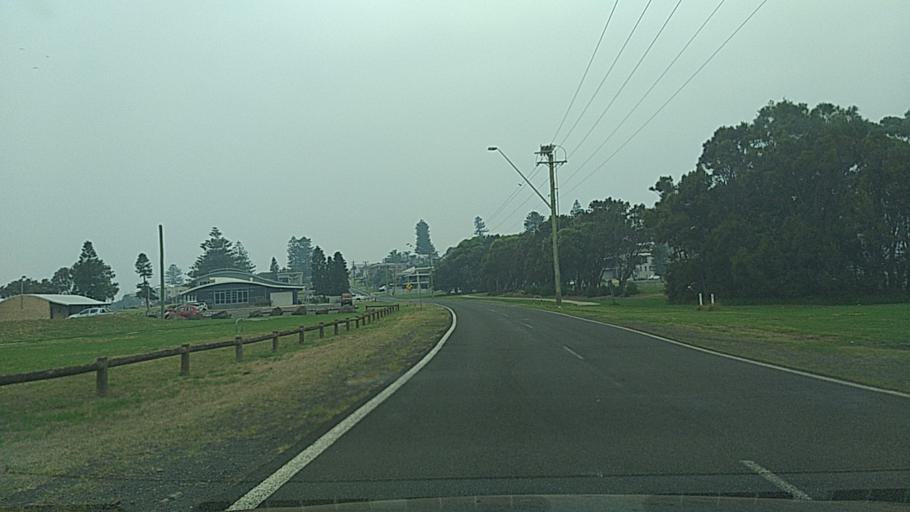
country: AU
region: New South Wales
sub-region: Shellharbour
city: Barrack Heights
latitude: -34.5706
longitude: 150.8664
